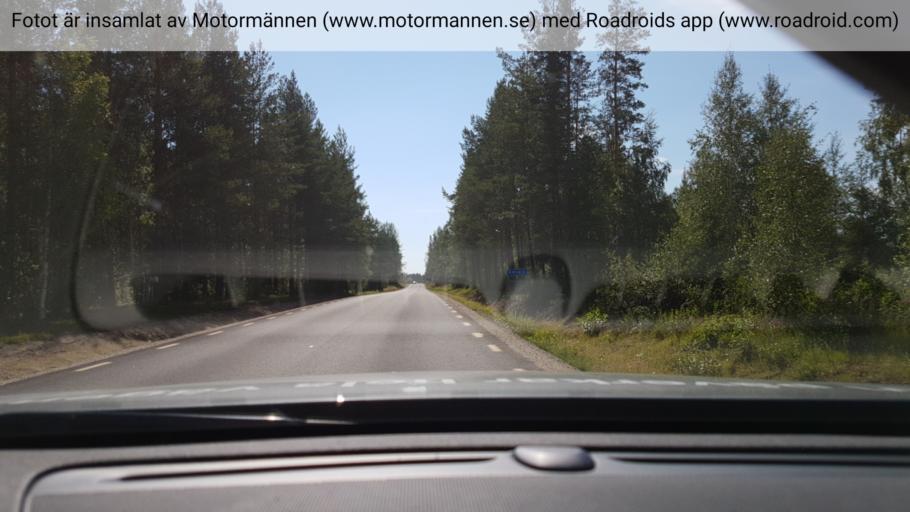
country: SE
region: Vaesterbotten
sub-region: Norsjo Kommun
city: Norsjoe
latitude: 64.5458
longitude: 19.3316
